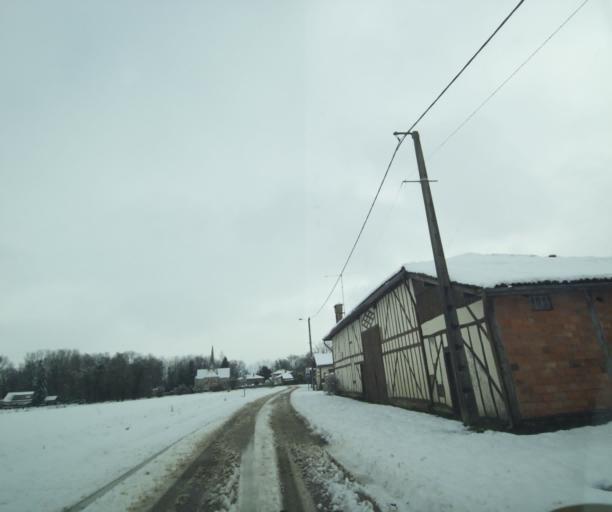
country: FR
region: Champagne-Ardenne
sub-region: Departement de la Haute-Marne
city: Montier-en-Der
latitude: 48.4966
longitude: 4.6980
